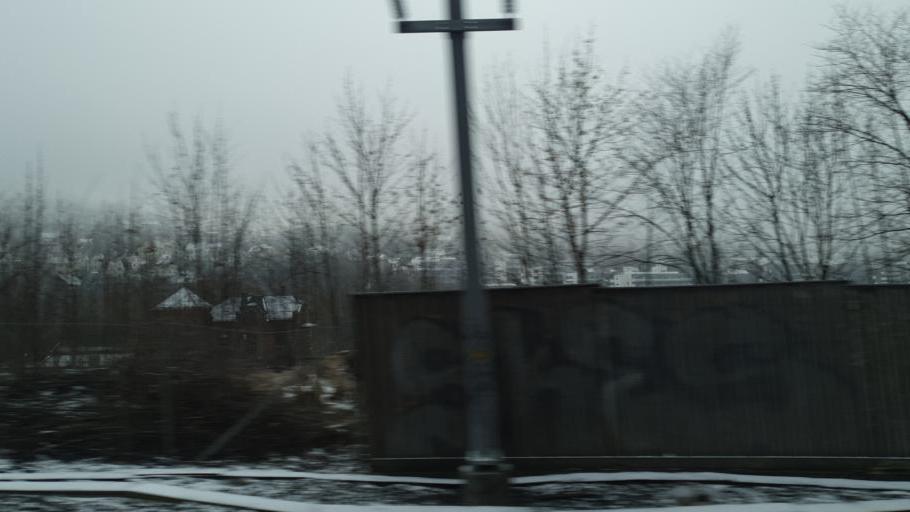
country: NO
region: Akershus
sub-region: Lorenskog
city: Kjenn
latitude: 59.9319
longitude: 10.9250
